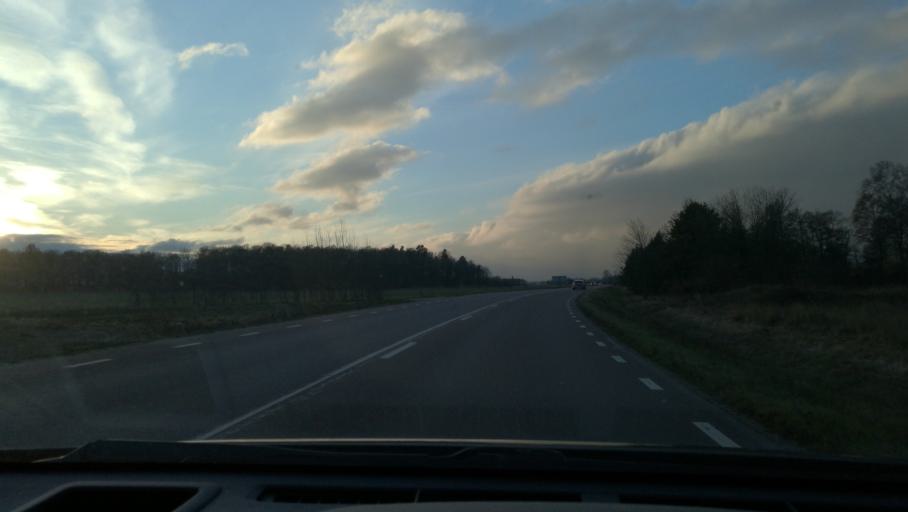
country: SE
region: Soedermanland
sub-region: Katrineholms Kommun
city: Katrineholm
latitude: 59.1552
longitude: 16.1061
